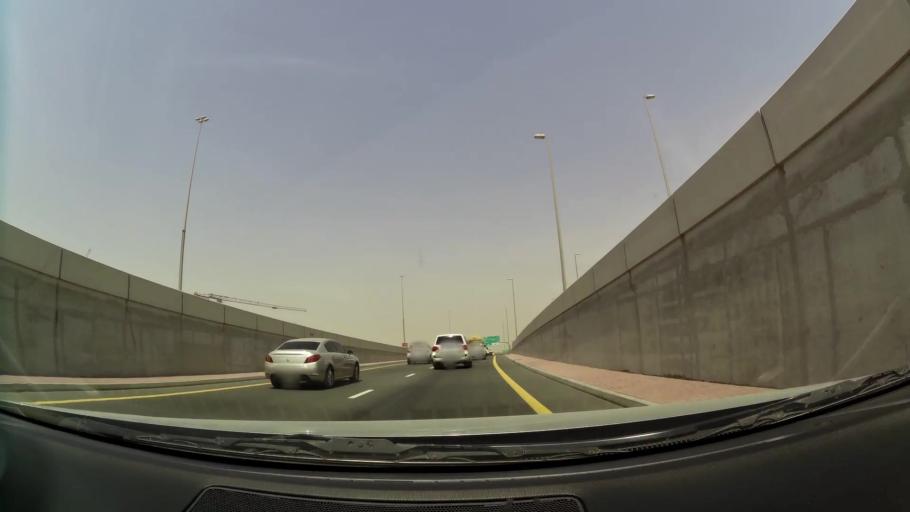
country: AE
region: Ash Shariqah
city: Sharjah
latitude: 25.2339
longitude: 55.4111
